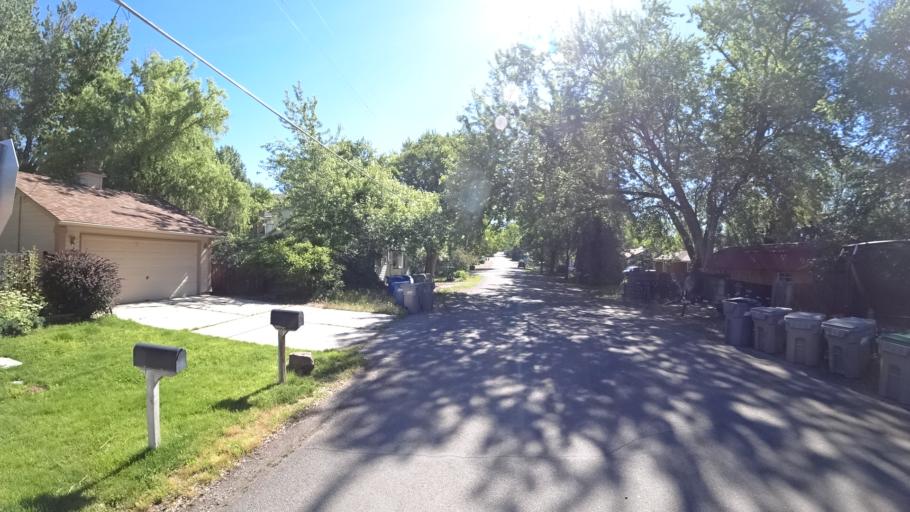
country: US
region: Idaho
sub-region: Ada County
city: Garden City
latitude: 43.6500
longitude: -116.2283
